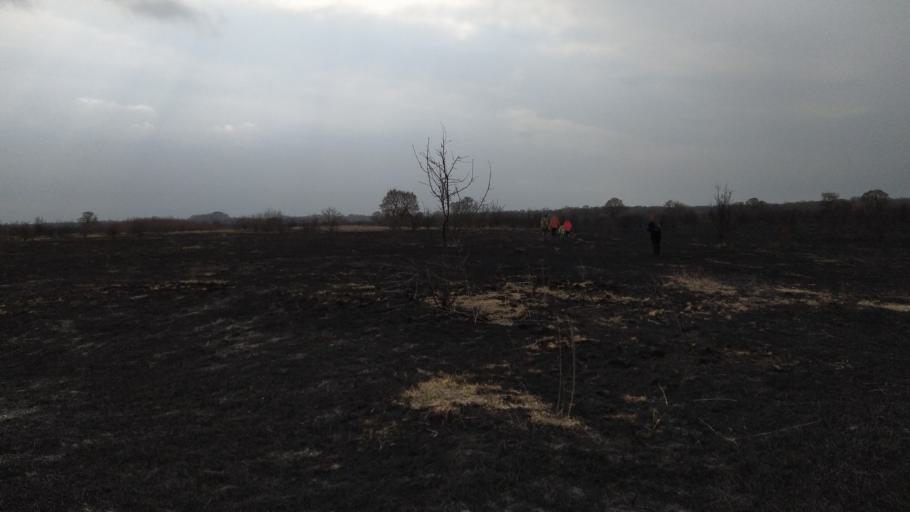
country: RU
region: Rostov
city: Semikarakorsk
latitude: 47.5517
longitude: 40.6761
